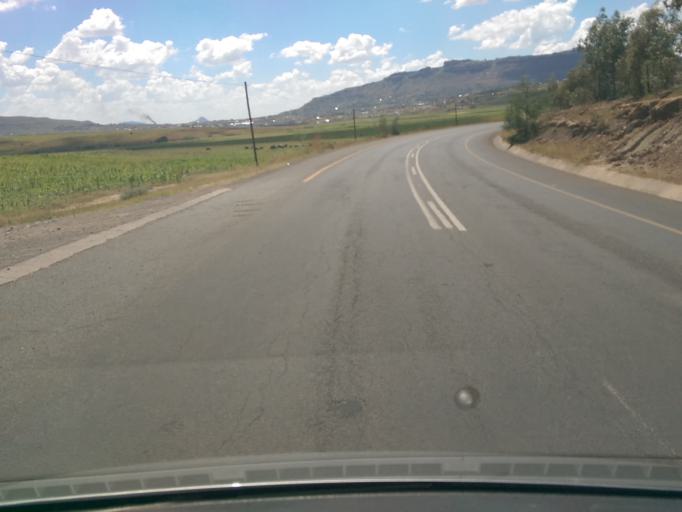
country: LS
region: Maseru
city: Maseru
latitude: -29.3930
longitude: 27.5047
